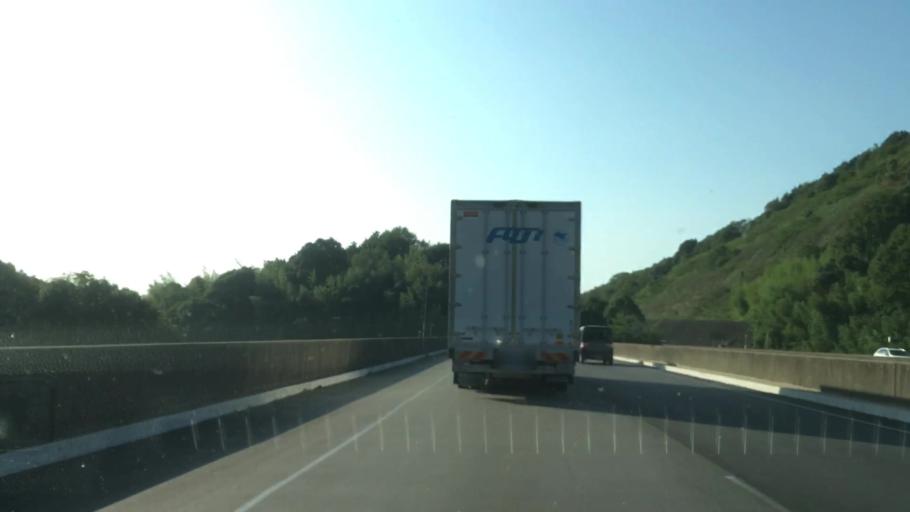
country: JP
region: Yamaguchi
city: Ogori-shimogo
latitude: 34.0835
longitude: 131.4764
